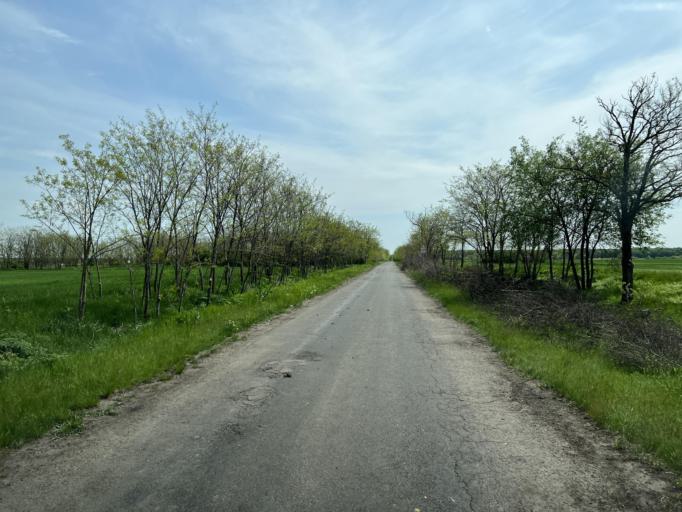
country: HU
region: Pest
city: Tapiogyorgye
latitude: 47.2934
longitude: 19.9978
